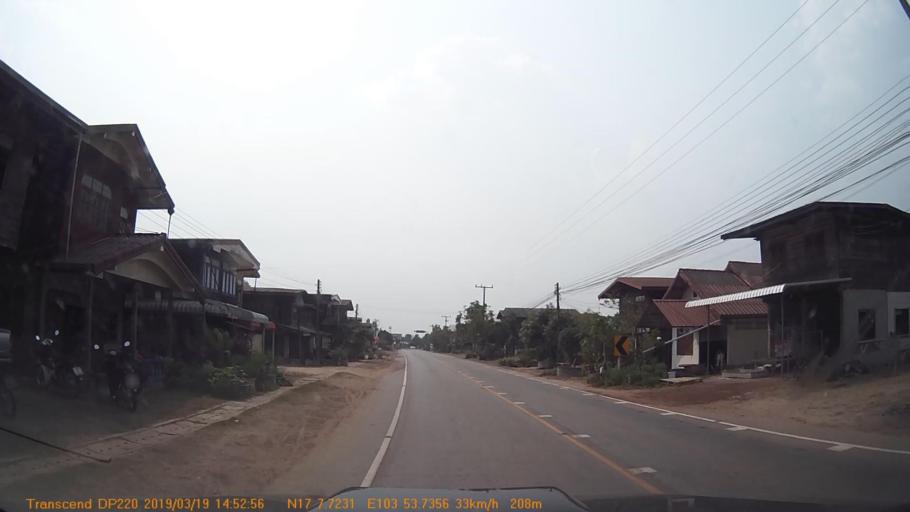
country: TH
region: Sakon Nakhon
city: Kut Bak
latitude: 17.1290
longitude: 103.8955
